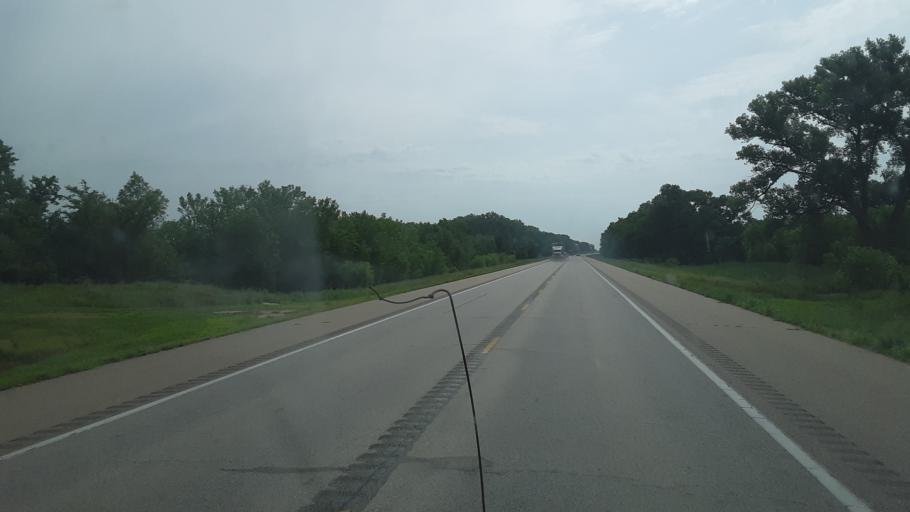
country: US
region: Kansas
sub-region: Stafford County
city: Stafford
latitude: 37.9845
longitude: -98.3760
